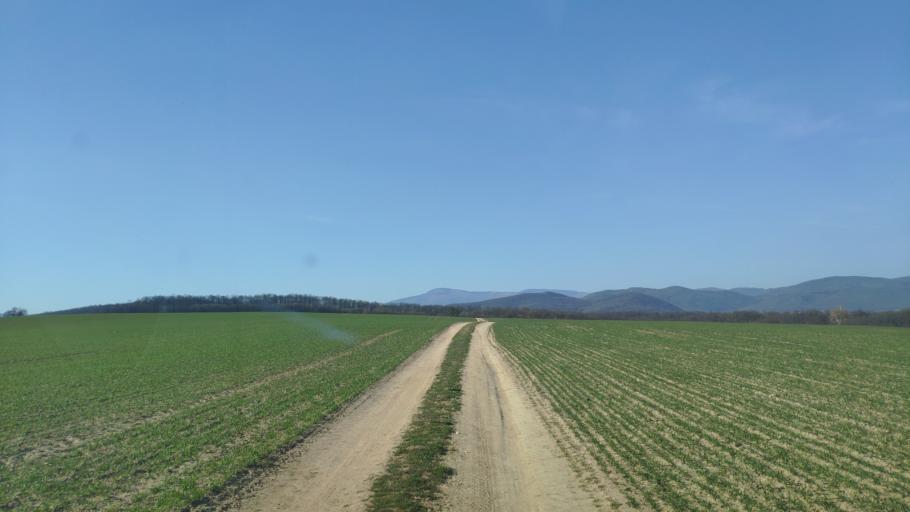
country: SK
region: Banskobystricky
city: Revuca
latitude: 48.5466
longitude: 20.2749
